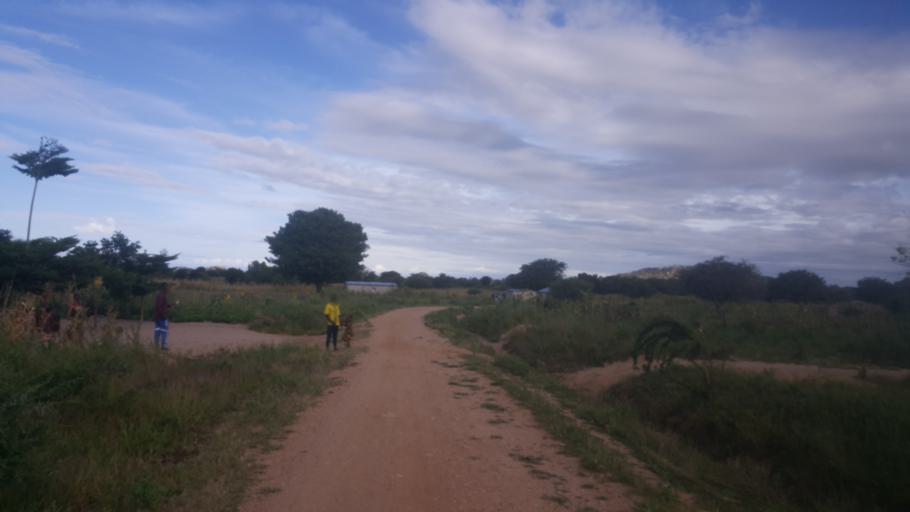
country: TZ
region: Dodoma
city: Dodoma
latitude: -6.0899
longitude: 35.5262
